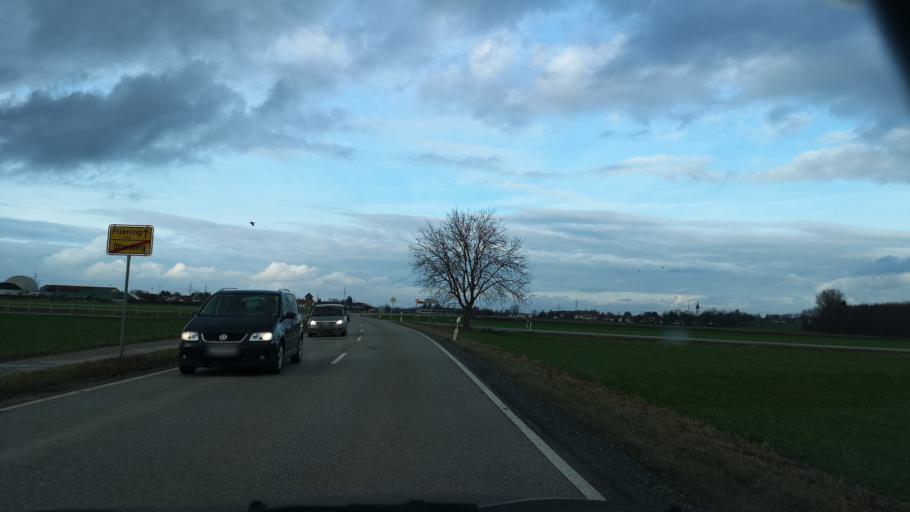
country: DE
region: Bavaria
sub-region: Upper Bavaria
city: Pliening
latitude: 48.1852
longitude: 11.8078
